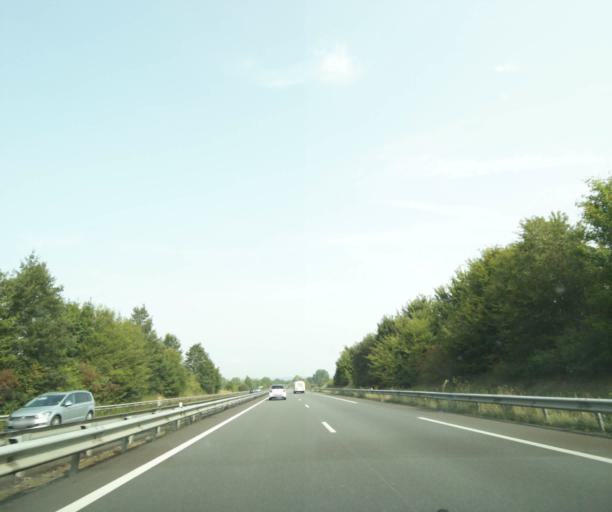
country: FR
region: Pays de la Loire
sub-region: Departement de la Sarthe
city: Saint-Paterne
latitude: 48.4333
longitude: 0.1374
